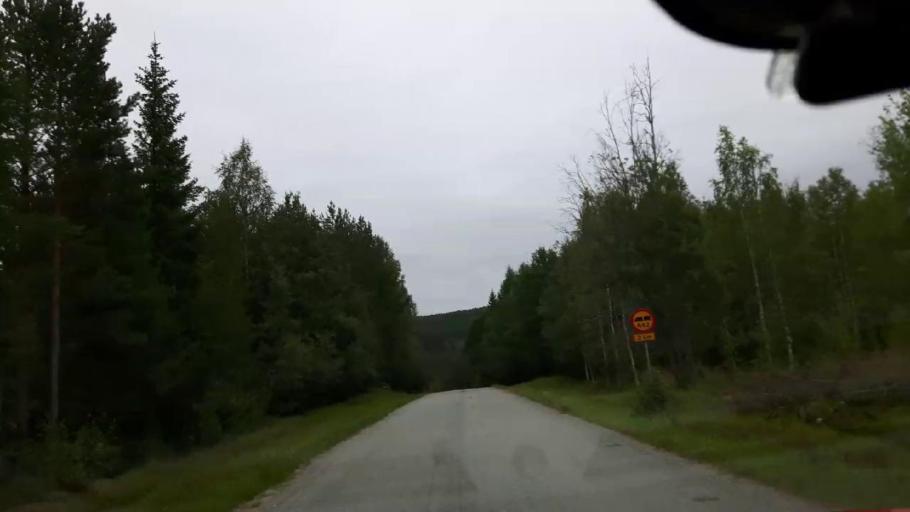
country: SE
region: Vaesternorrland
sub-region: Ange Kommun
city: Fransta
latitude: 62.7776
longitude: 15.9868
